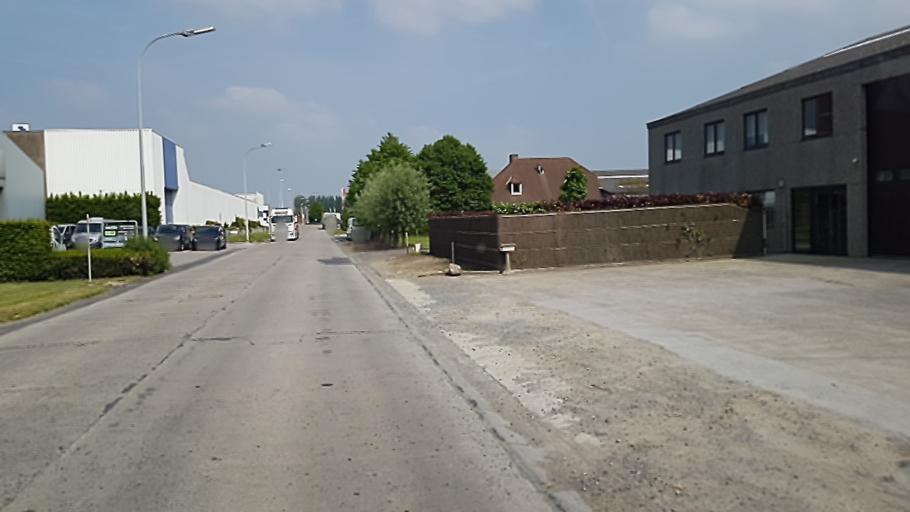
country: BE
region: Flanders
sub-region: Provincie West-Vlaanderen
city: Wevelgem
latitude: 50.8479
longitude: 3.1817
